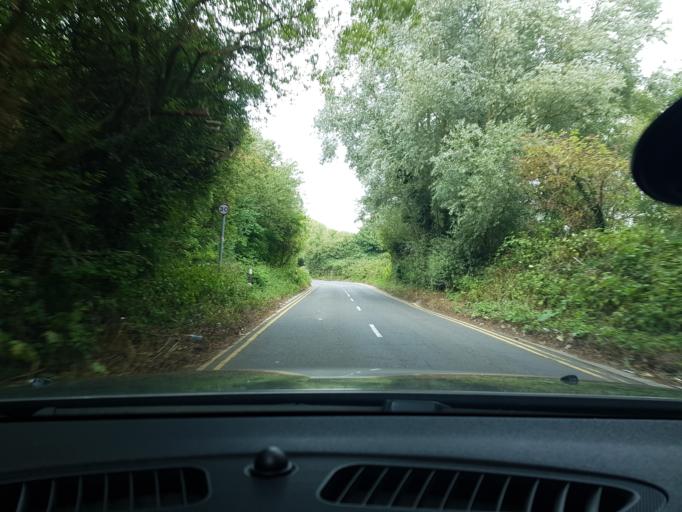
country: GB
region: England
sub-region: Buckinghamshire
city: Iver
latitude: 51.4860
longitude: -0.4896
